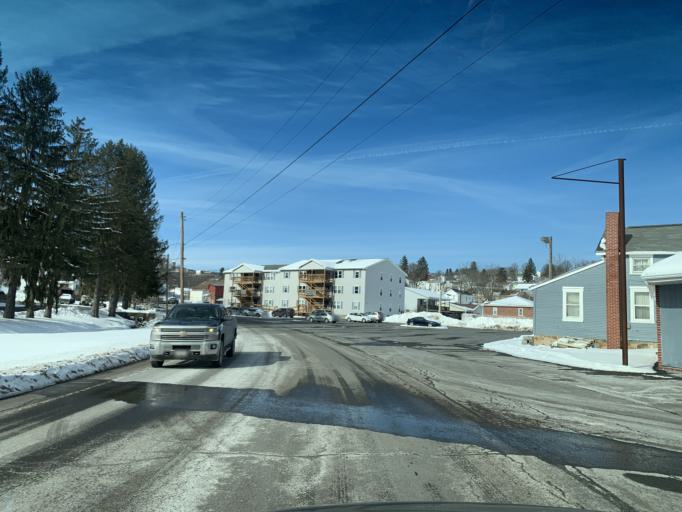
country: US
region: Maryland
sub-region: Allegany County
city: Frostburg
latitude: 39.6495
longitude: -78.9223
